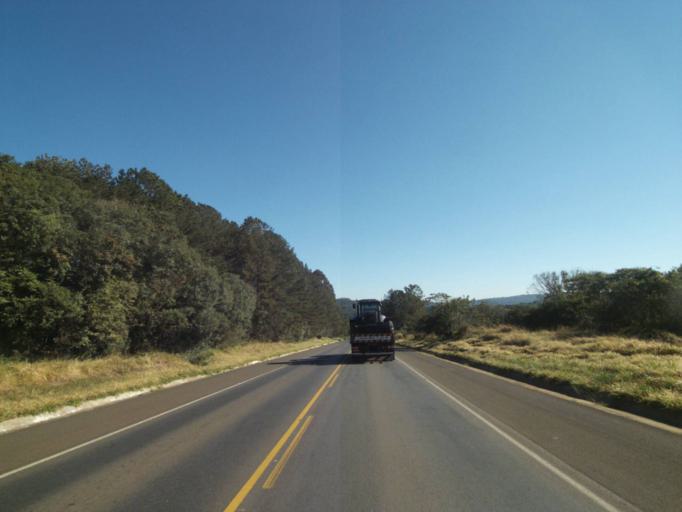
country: BR
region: Parana
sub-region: Tibagi
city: Tibagi
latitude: -24.4847
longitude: -50.4398
